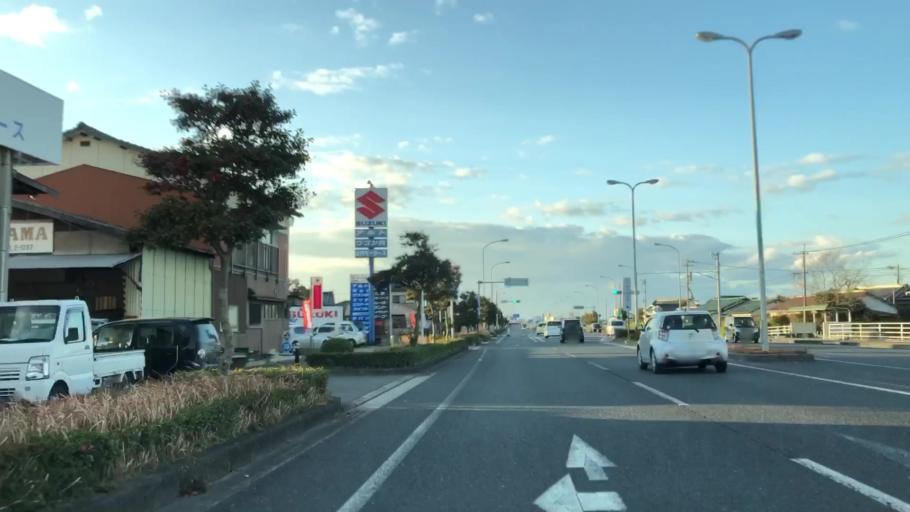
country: JP
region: Fukuoka
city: Nakatsu
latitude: 33.5461
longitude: 131.2828
